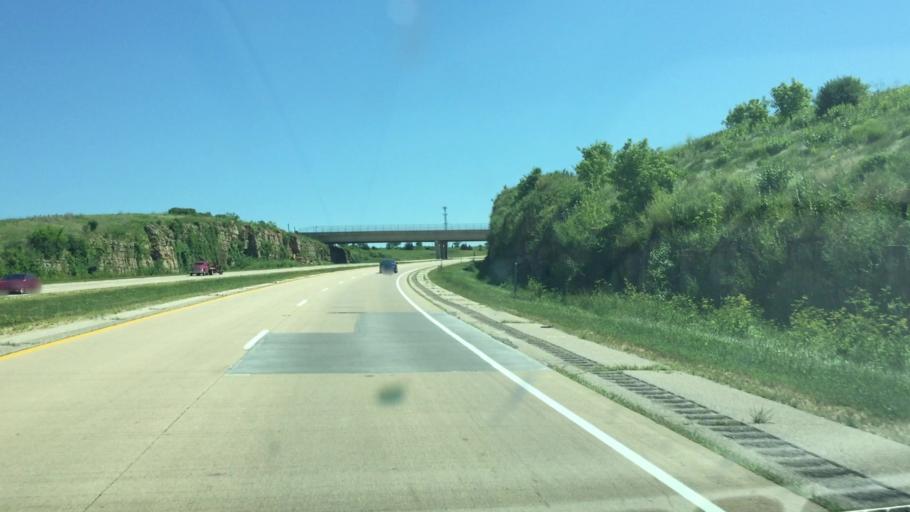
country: US
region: Wisconsin
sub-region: Iowa County
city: Mineral Point
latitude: 42.8509
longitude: -90.1991
